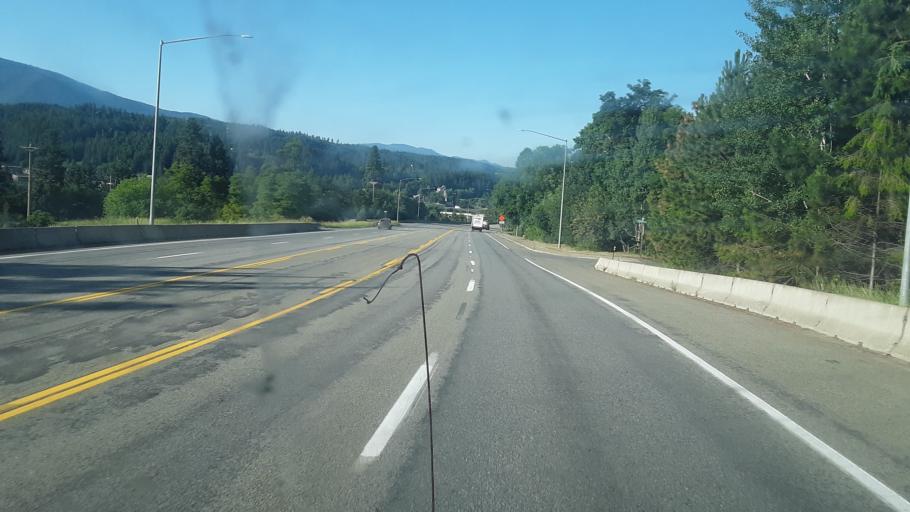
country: US
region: Idaho
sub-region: Boundary County
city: Bonners Ferry
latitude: 48.7074
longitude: -116.3101
